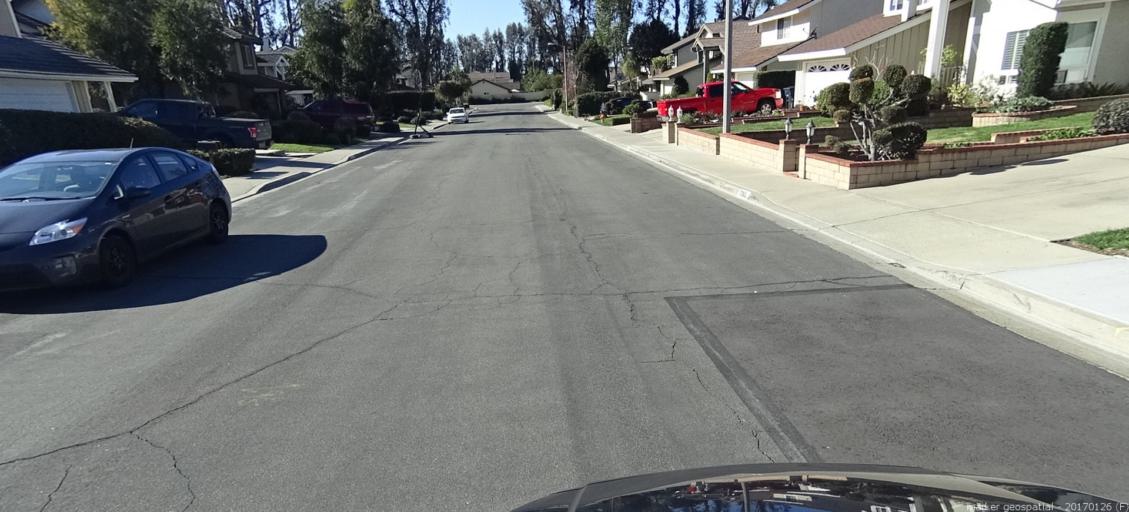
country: US
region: California
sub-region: Orange County
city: Lake Forest
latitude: 33.6313
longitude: -117.6829
